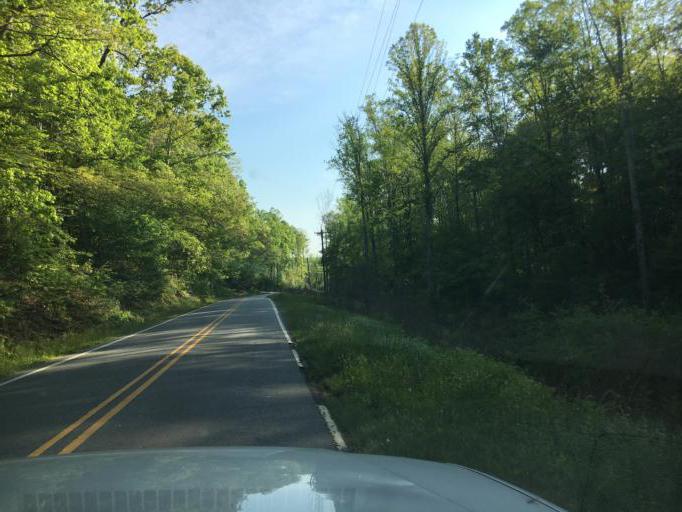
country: US
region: North Carolina
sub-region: Rutherford County
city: Rutherfordton
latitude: 35.3032
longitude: -82.0054
